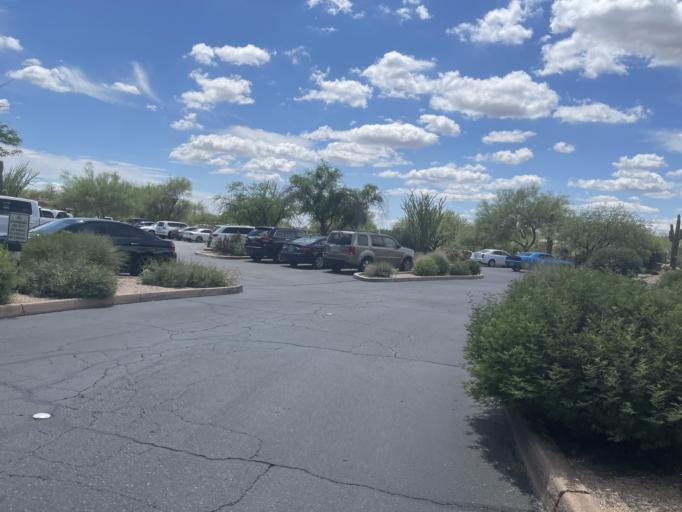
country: US
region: Arizona
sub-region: Maricopa County
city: Carefree
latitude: 33.8020
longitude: -111.9186
